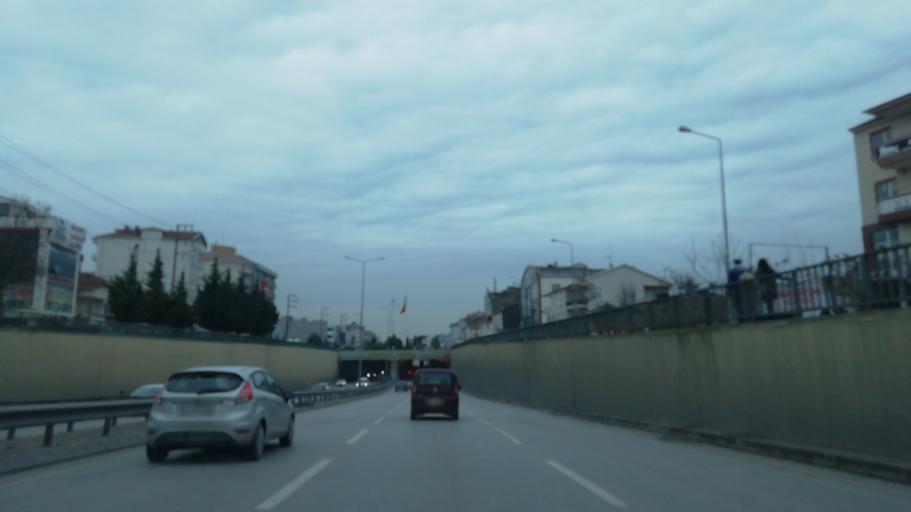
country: TR
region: Kocaeli
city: Derince
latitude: 40.7561
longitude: 29.8260
